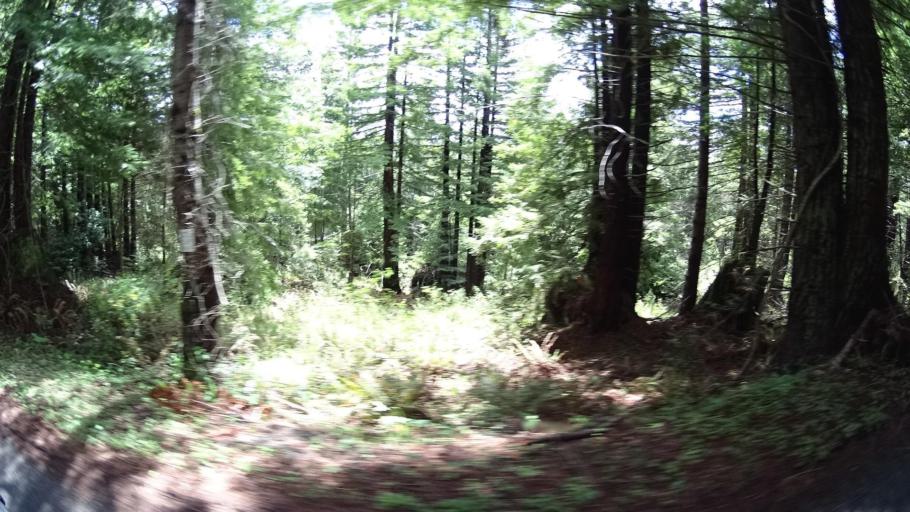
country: US
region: California
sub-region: Humboldt County
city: Blue Lake
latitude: 40.8444
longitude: -123.9220
